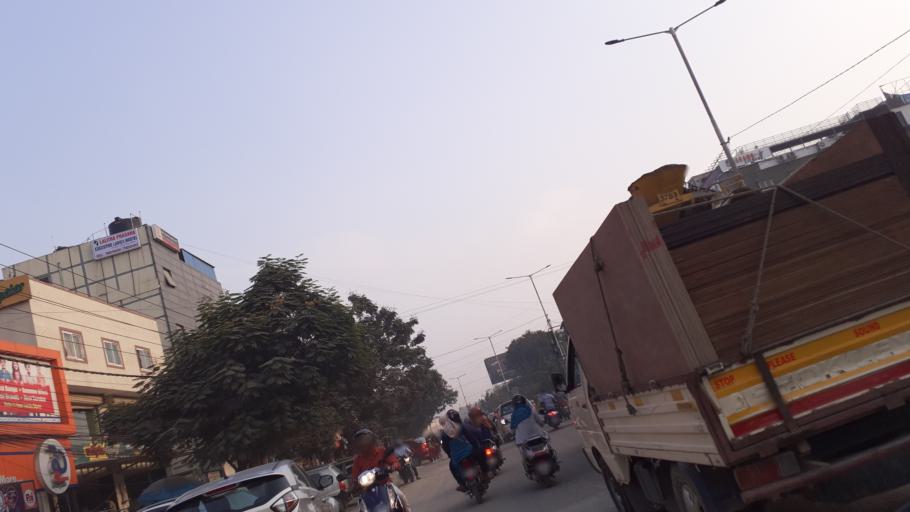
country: IN
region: Telangana
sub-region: Rangareddi
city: Kukatpalli
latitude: 17.4704
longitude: 78.3654
